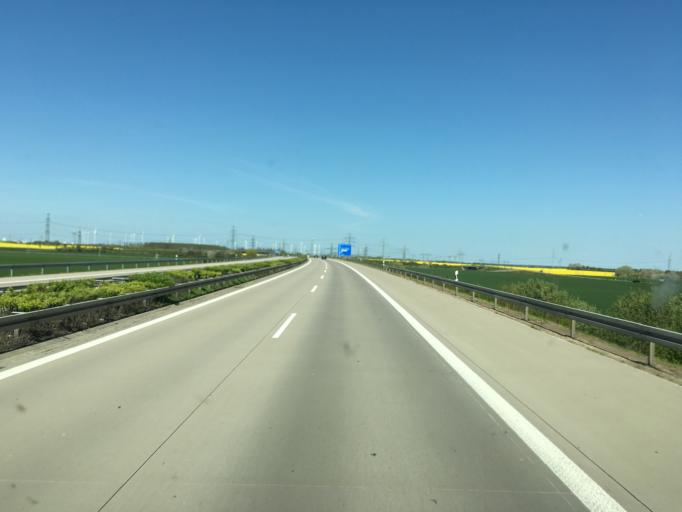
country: DE
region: Saxony-Anhalt
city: Bad Lauchstadt
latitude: 51.3876
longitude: 11.9086
